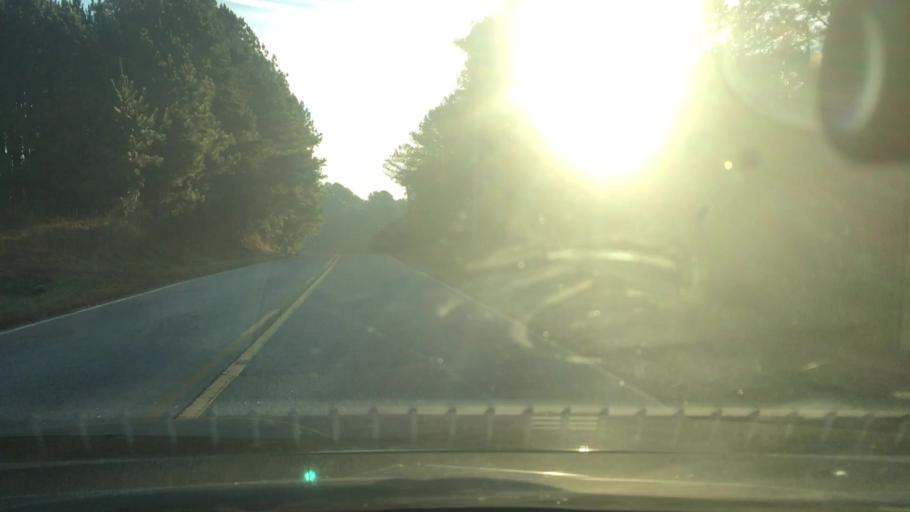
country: US
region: Georgia
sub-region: Spalding County
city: Experiment
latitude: 33.2623
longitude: -84.3019
